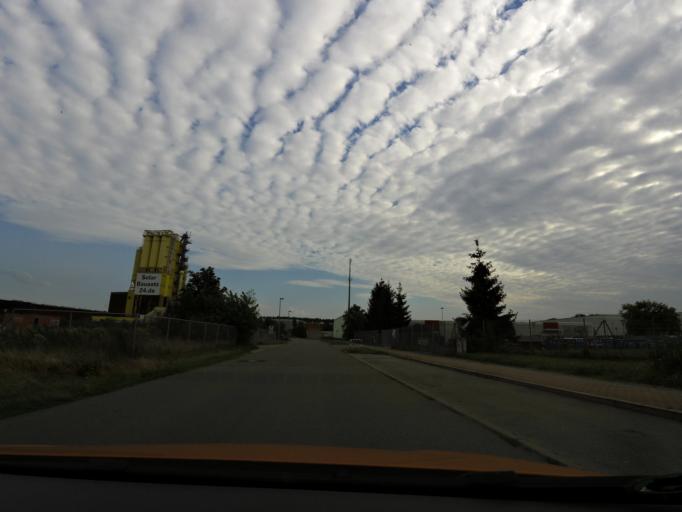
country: DE
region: Brandenburg
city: Brandenburg an der Havel
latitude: 52.3792
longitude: 12.5970
